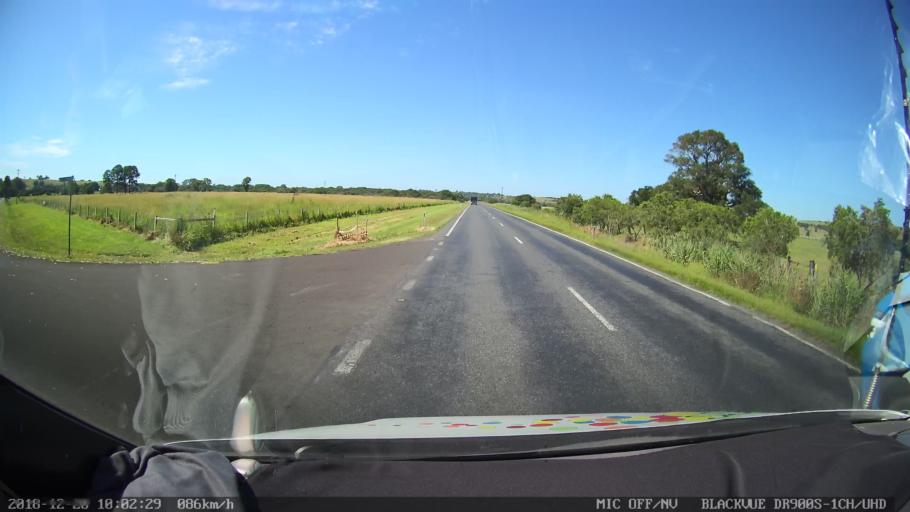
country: AU
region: New South Wales
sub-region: Lismore Municipality
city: East Lismore
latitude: -28.8588
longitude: 153.2614
